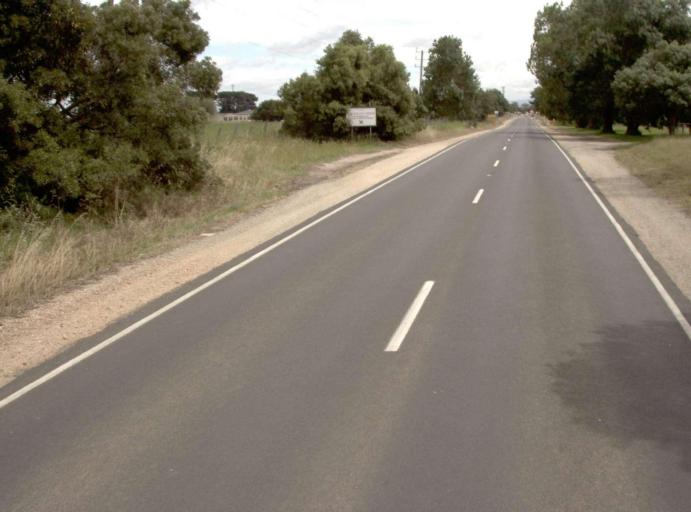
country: AU
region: Victoria
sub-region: Wellington
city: Sale
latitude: -37.9795
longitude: 146.9892
